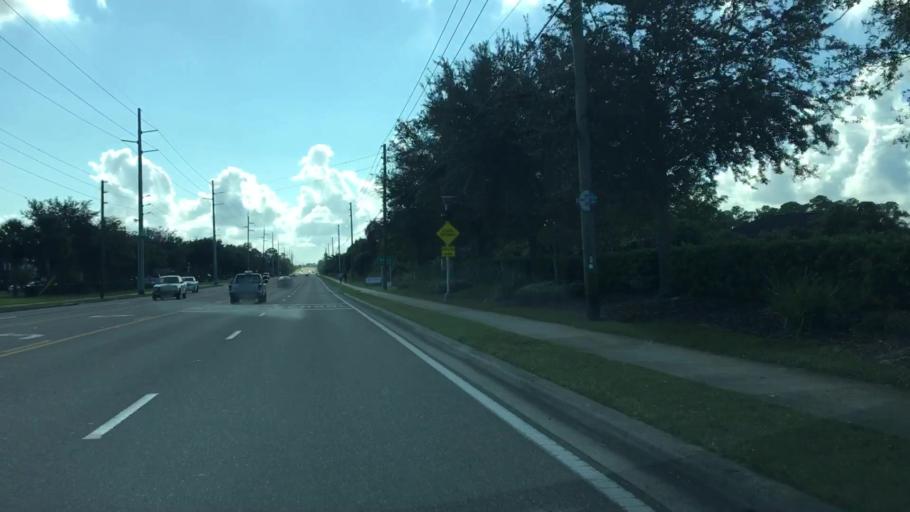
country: US
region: Florida
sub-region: Volusia County
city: Deltona
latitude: 28.8981
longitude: -81.2852
